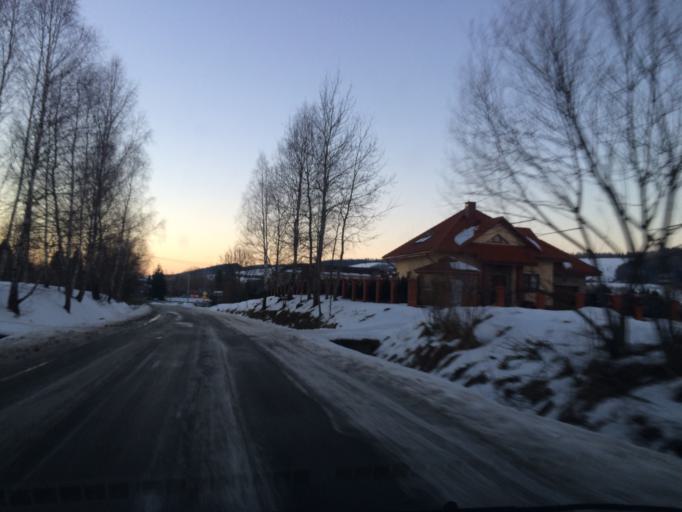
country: PL
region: Subcarpathian Voivodeship
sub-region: Powiat bieszczadzki
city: Ustrzyki Dolne
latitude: 49.4158
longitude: 22.5743
